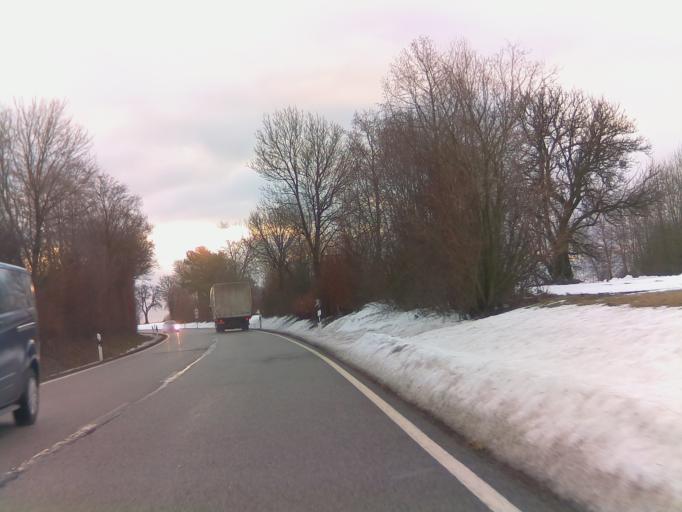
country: DE
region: Baden-Wuerttemberg
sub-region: Karlsruhe Region
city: Fahrenbach
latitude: 49.4604
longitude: 9.0969
